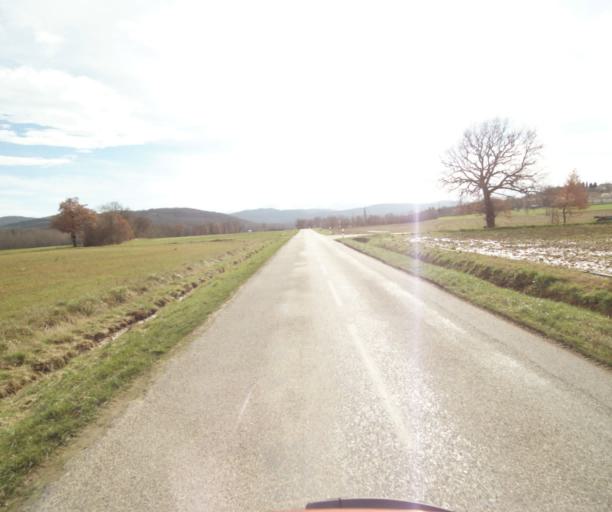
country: FR
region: Midi-Pyrenees
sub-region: Departement de l'Ariege
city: La Tour-du-Crieu
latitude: 43.0833
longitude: 1.7410
